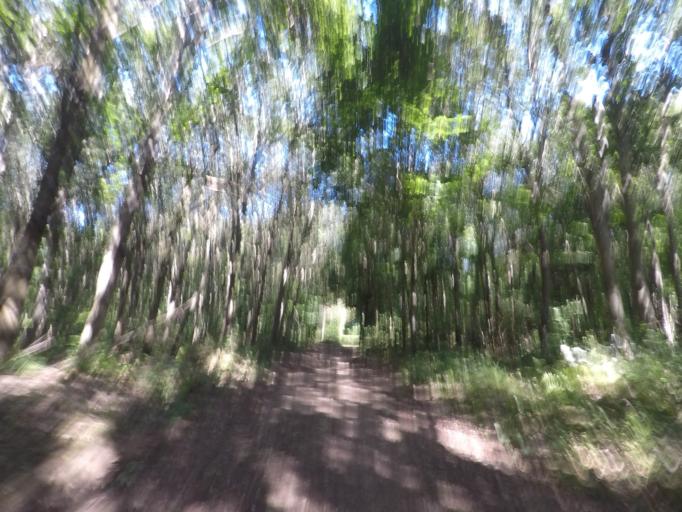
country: LU
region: Luxembourg
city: Bridel
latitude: 49.6545
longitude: 6.0747
